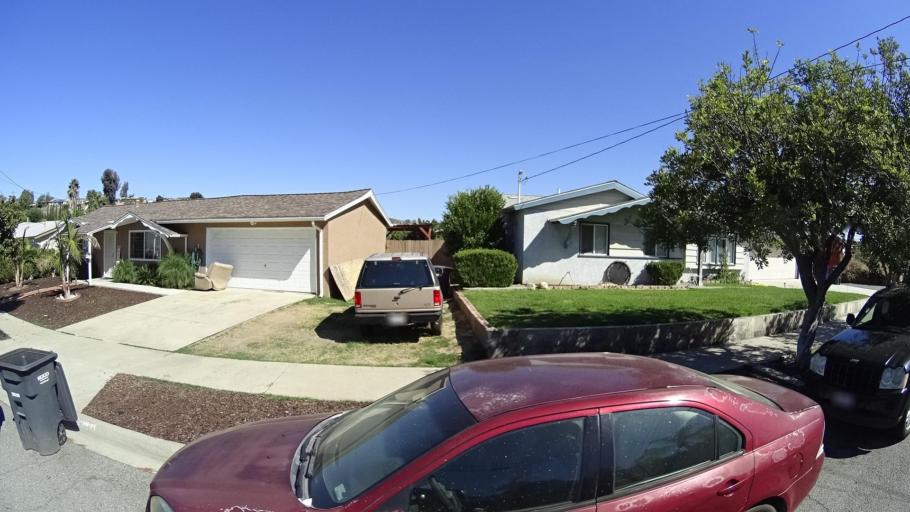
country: US
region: California
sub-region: San Diego County
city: La Presa
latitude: 32.7161
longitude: -117.0226
